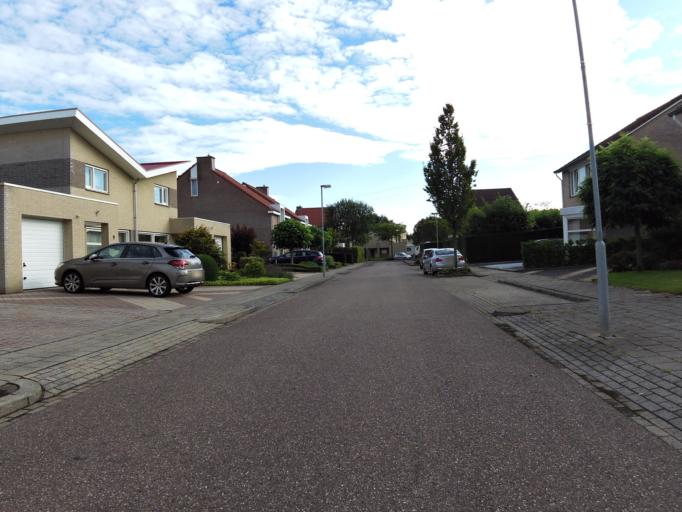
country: NL
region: Limburg
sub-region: Gemeente Voerendaal
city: Klimmen
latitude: 50.8810
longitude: 5.8756
